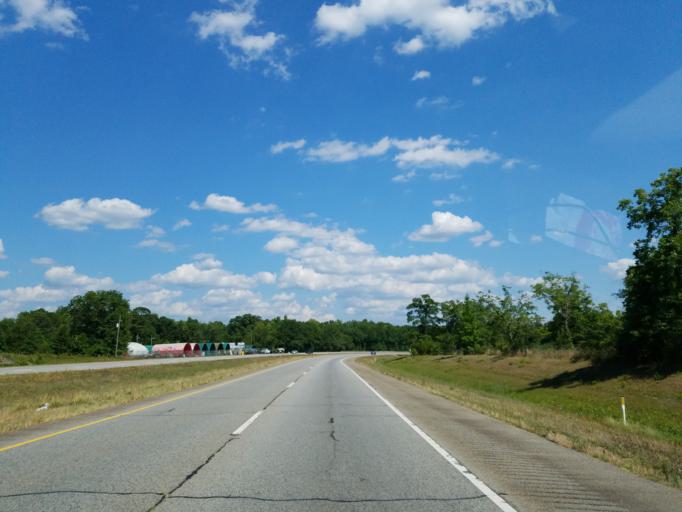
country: US
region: Georgia
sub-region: Lamar County
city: Barnesville
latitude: 33.1003
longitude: -84.1830
